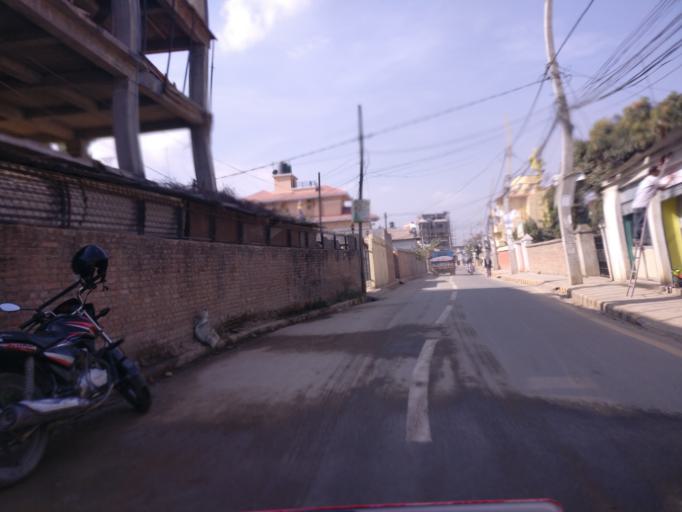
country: NP
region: Central Region
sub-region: Bagmati Zone
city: Patan
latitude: 27.6664
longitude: 85.3156
